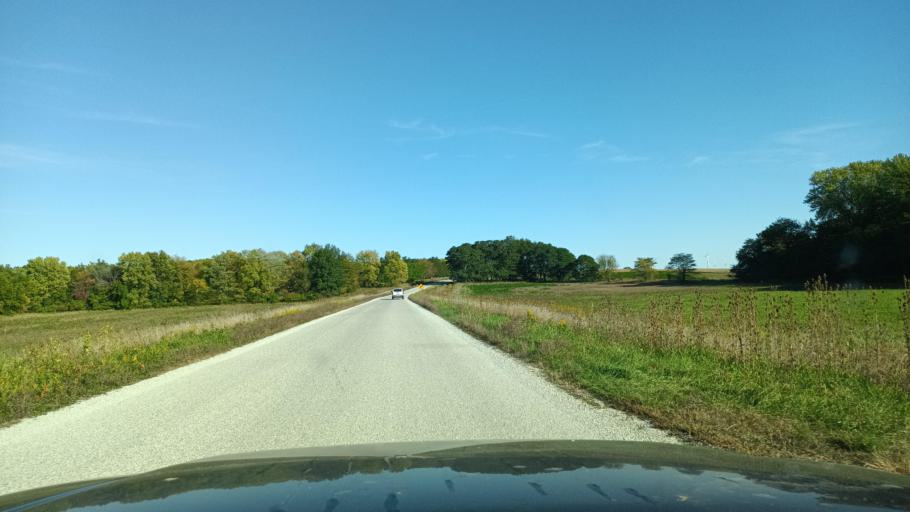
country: US
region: Illinois
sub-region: Logan County
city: Atlanta
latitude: 40.2377
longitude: -89.1671
